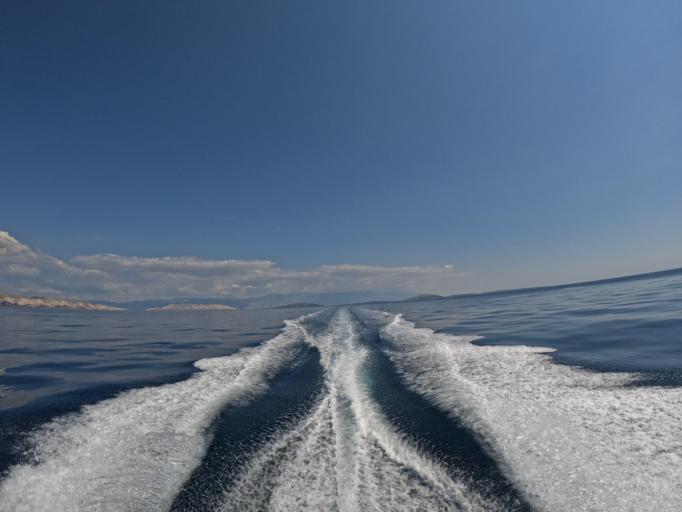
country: HR
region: Primorsko-Goranska
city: Punat
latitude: 44.9147
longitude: 14.5820
